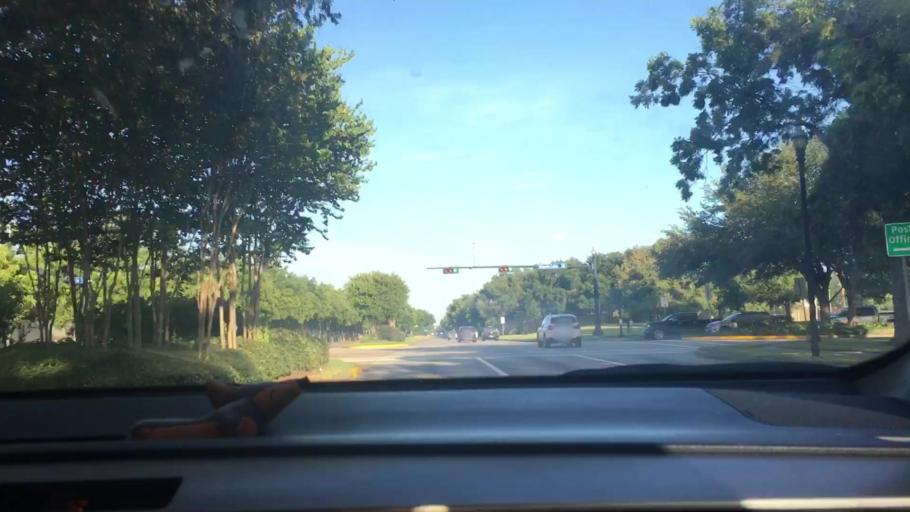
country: US
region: Texas
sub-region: Fort Bend County
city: Sugar Land
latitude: 29.5942
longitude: -95.6112
